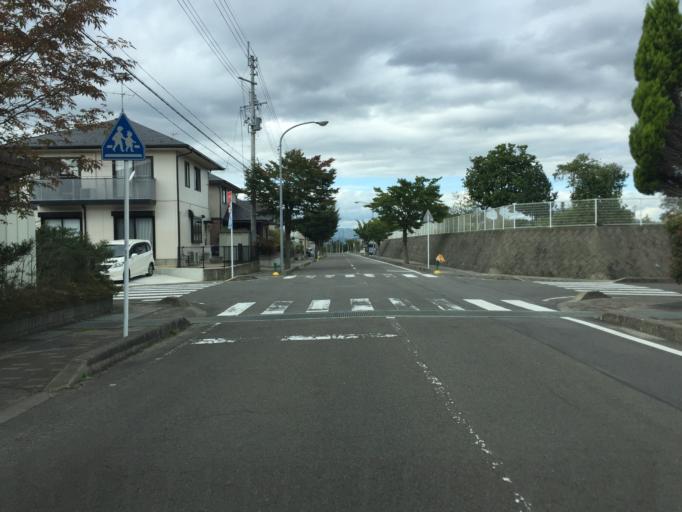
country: JP
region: Fukushima
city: Fukushima-shi
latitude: 37.7141
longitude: 140.4713
